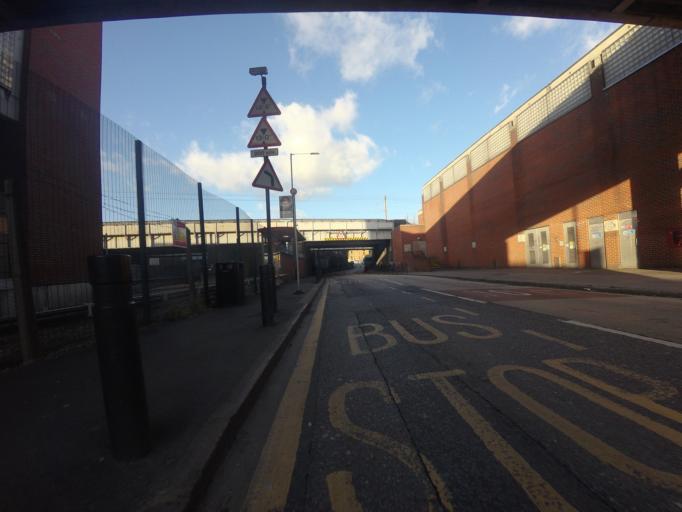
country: GB
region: England
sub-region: Greater London
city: Poplar
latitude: 51.5280
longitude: 0.0048
